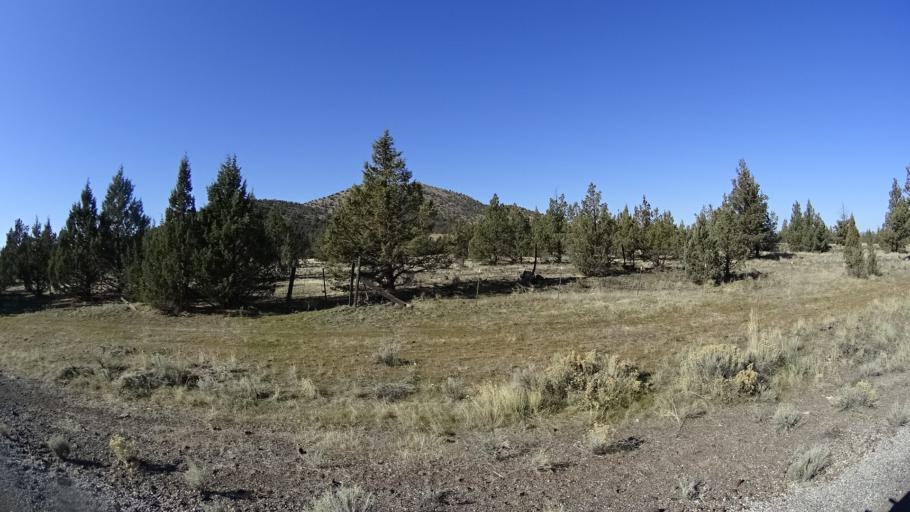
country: US
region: California
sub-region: Siskiyou County
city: Montague
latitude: 41.6715
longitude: -122.3699
